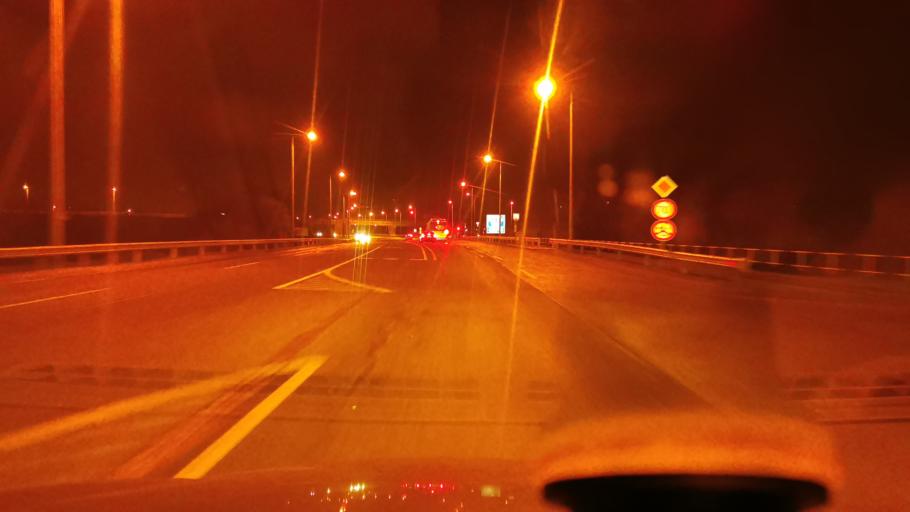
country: HU
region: Hajdu-Bihar
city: Debrecen
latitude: 47.5755
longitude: 21.5916
